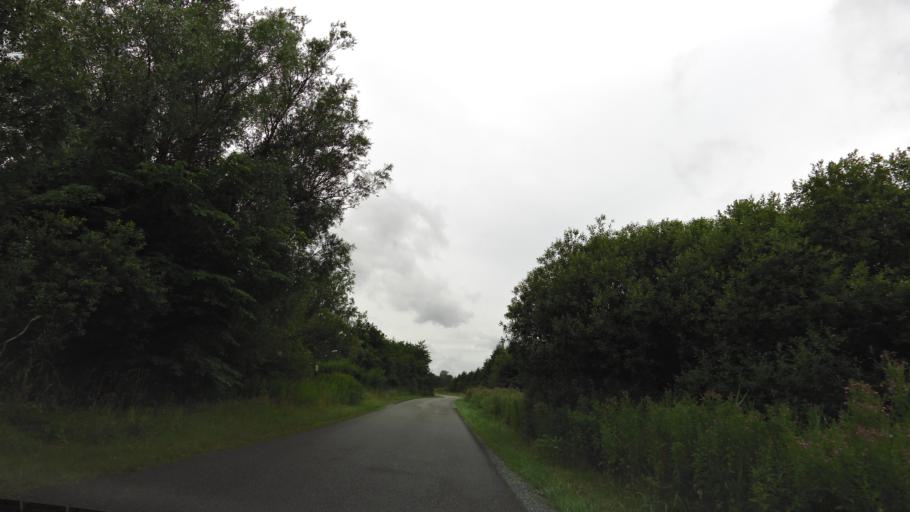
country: DK
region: South Denmark
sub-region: Nordfyns Kommune
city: Otterup
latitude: 55.5557
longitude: 10.3989
